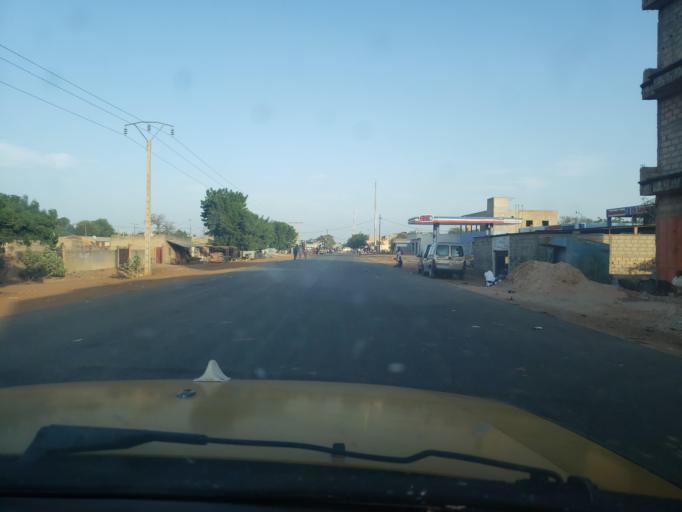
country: SN
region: Louga
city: Dara
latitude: 15.3496
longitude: -15.4907
